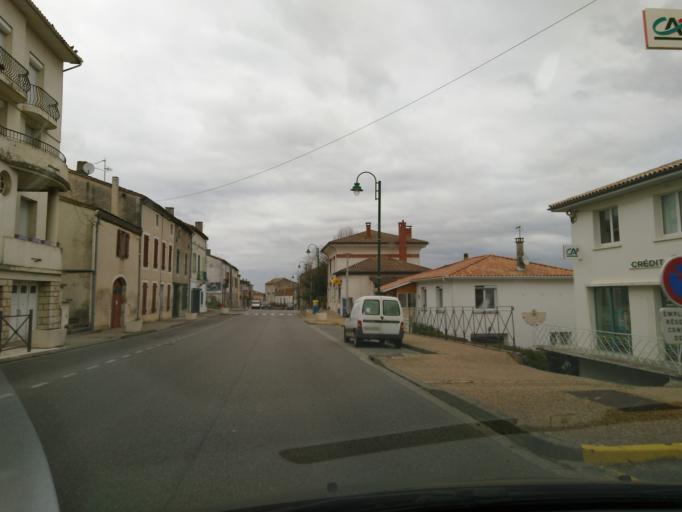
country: FR
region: Aquitaine
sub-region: Departement du Lot-et-Garonne
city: Cancon
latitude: 44.5335
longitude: 0.6254
